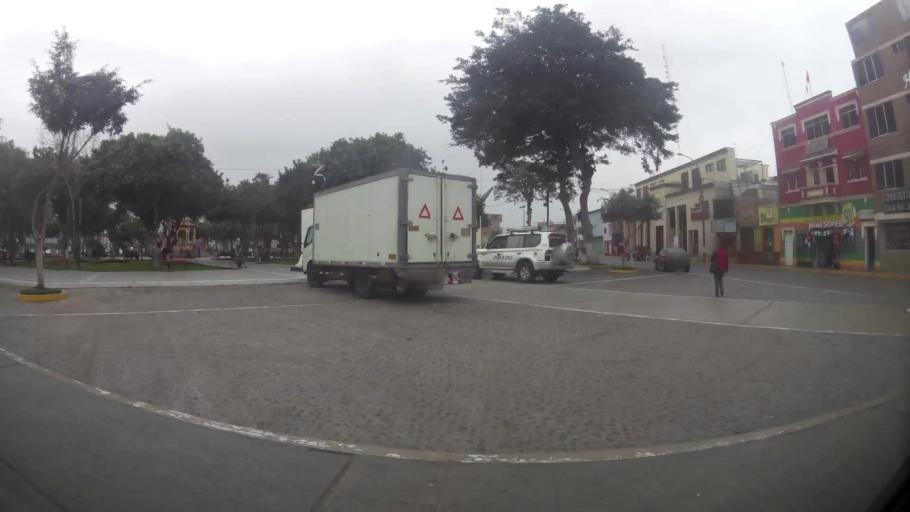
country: PE
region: Lima
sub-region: Provincia de Huaral
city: Chancay
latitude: -11.5625
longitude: -77.2706
